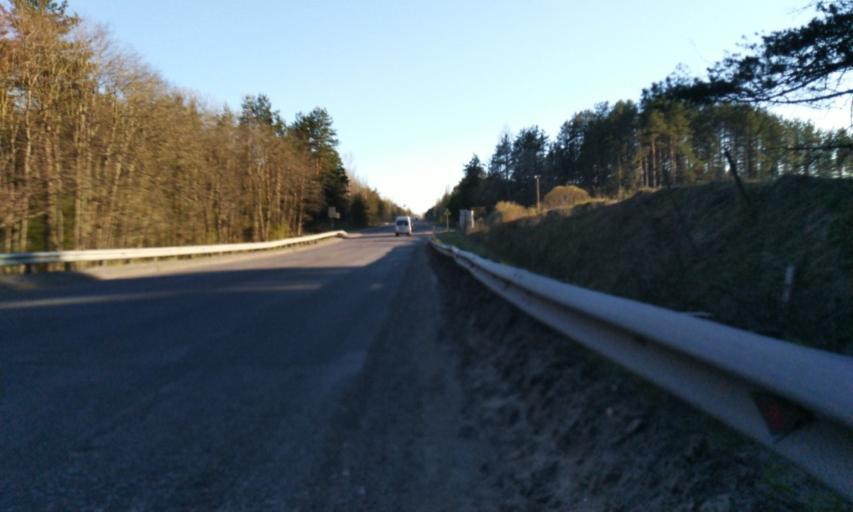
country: RU
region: Leningrad
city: Toksovo
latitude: 60.1299
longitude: 30.5205
